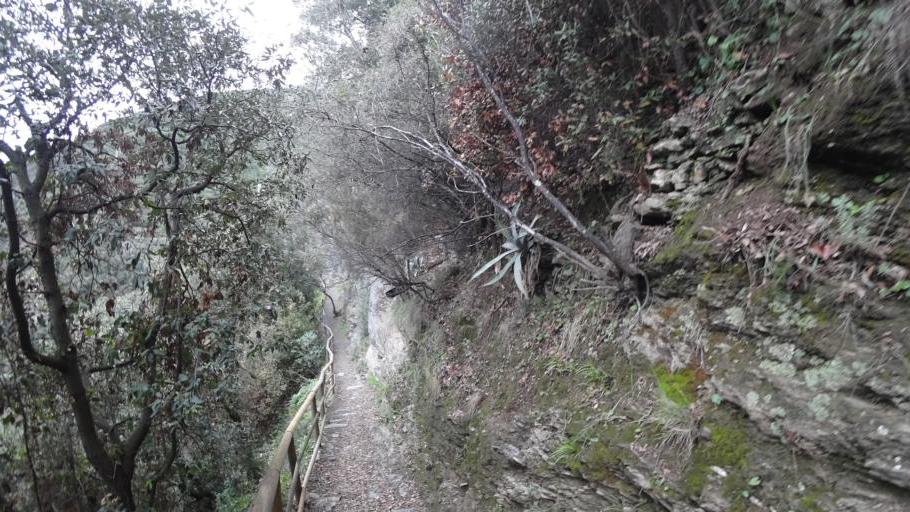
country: IT
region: Liguria
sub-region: Provincia di La Spezia
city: Vernazza
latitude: 44.1396
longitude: 9.6774
